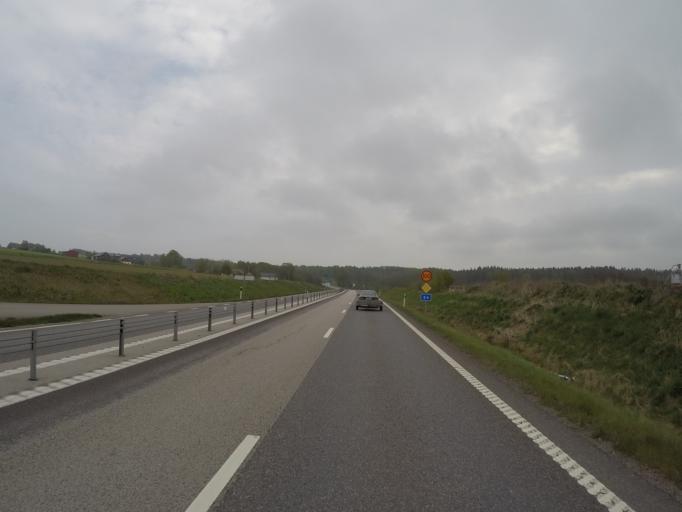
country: SE
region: Halland
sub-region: Laholms Kommun
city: Laholm
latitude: 56.4703
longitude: 13.0843
